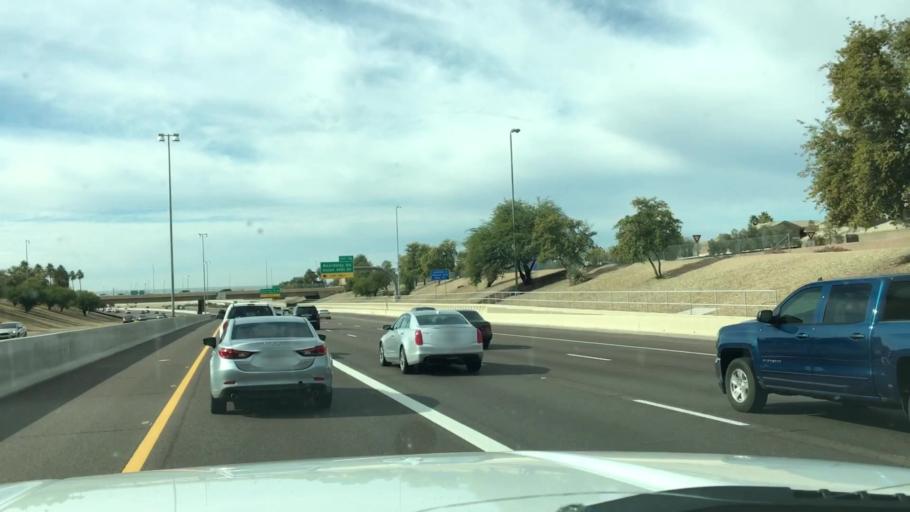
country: US
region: Arizona
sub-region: Maricopa County
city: Sun City
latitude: 33.6659
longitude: -112.2169
